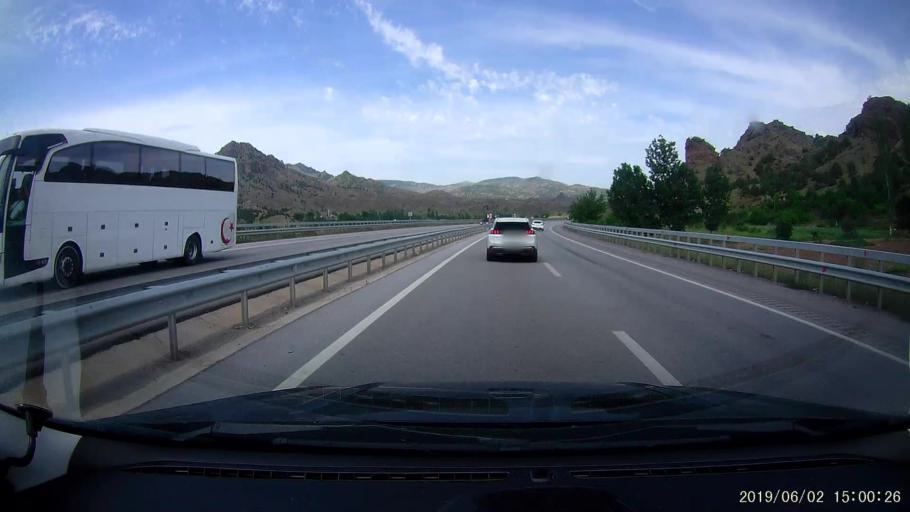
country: TR
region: Corum
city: Osmancik
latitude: 40.9791
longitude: 34.7126
